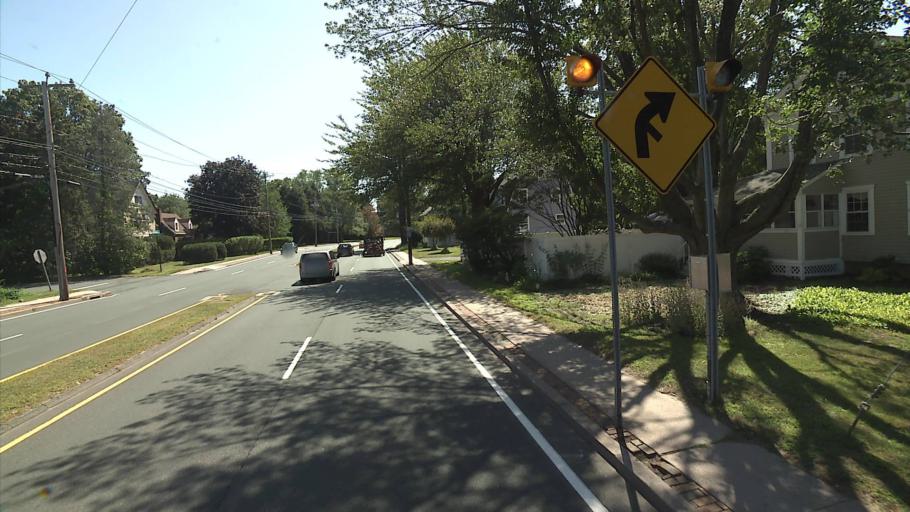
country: US
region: Connecticut
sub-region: Hartford County
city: Windsor
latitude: 41.8332
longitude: -72.6543
